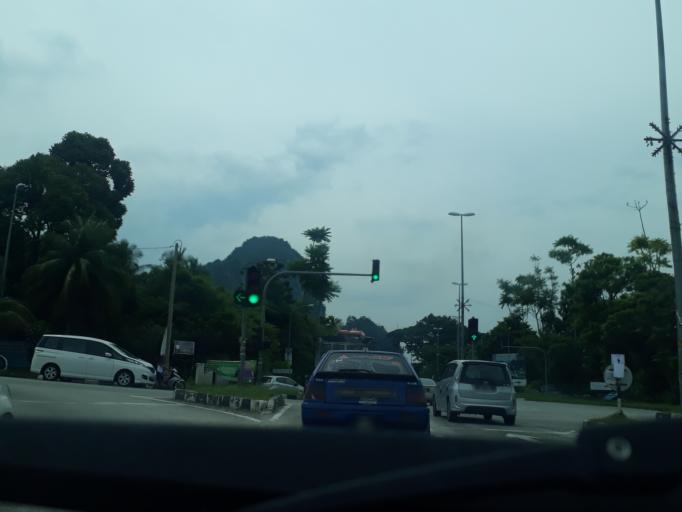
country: MY
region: Perak
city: Ipoh
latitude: 4.6369
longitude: 101.1547
